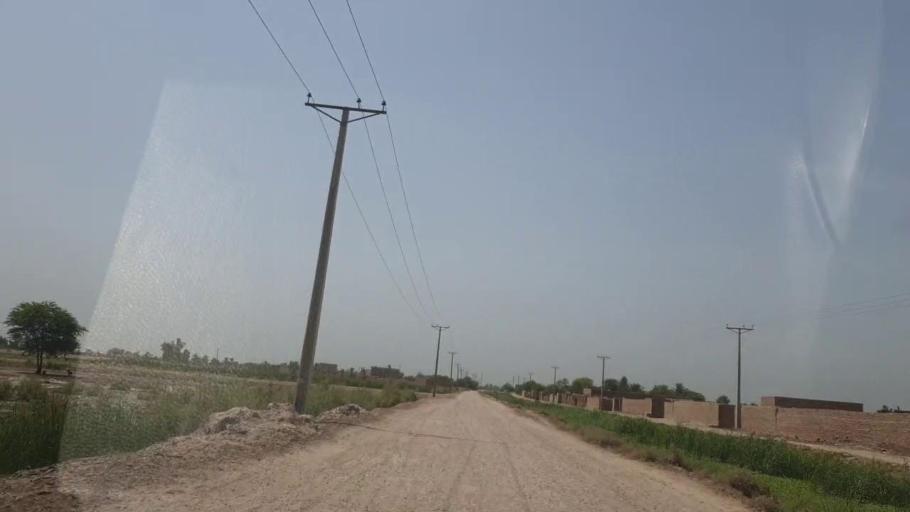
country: PK
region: Sindh
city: Ranipur
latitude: 27.2989
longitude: 68.5454
